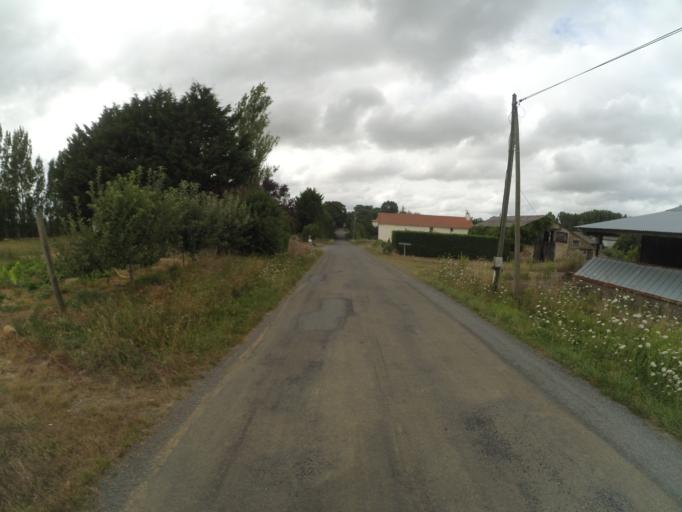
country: FR
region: Pays de la Loire
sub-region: Departement de la Vendee
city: Saint-Philbert-de-Bouaine
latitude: 47.0126
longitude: -1.5481
